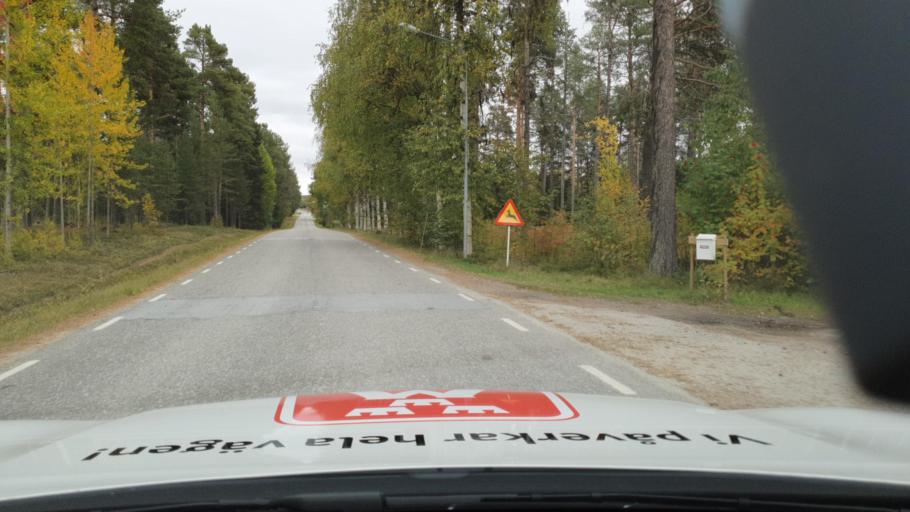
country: SE
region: Vaesterbotten
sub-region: Asele Kommun
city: Asele
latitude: 64.1586
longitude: 17.3294
